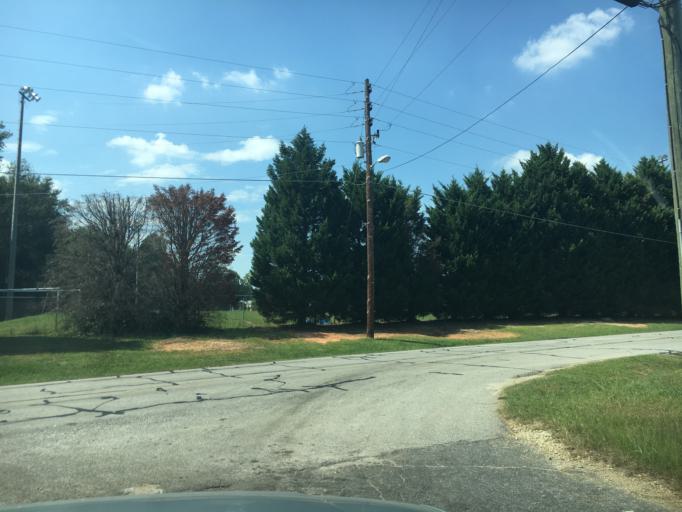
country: US
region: Georgia
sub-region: Hart County
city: Hartwell
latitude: 34.3483
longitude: -82.9190
